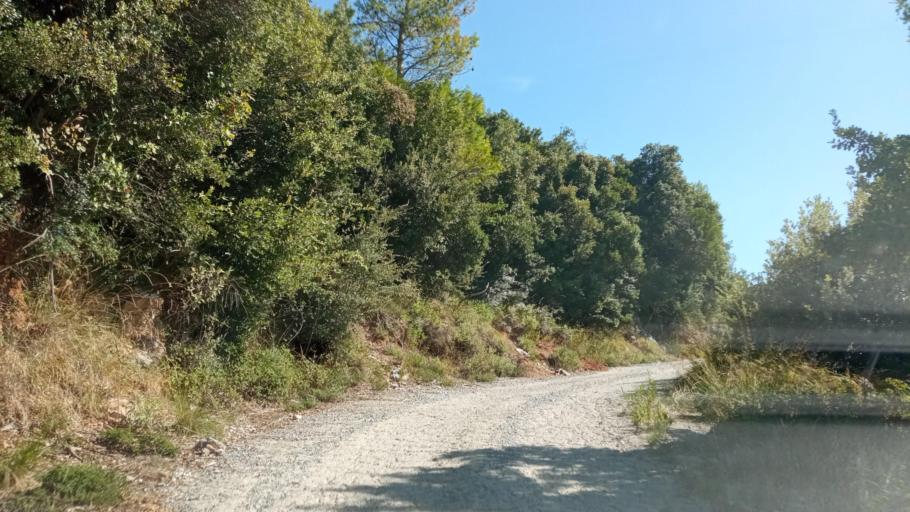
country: GR
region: Central Greece
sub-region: Nomos Evvoias
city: Kymi
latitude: 38.6512
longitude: 23.9038
